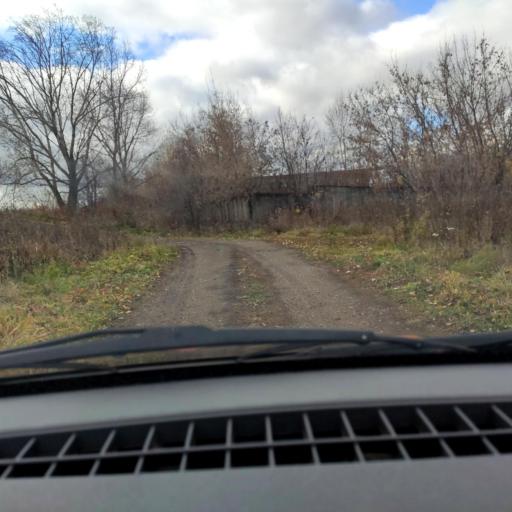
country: RU
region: Bashkortostan
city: Ufa
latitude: 54.5784
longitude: 55.9101
